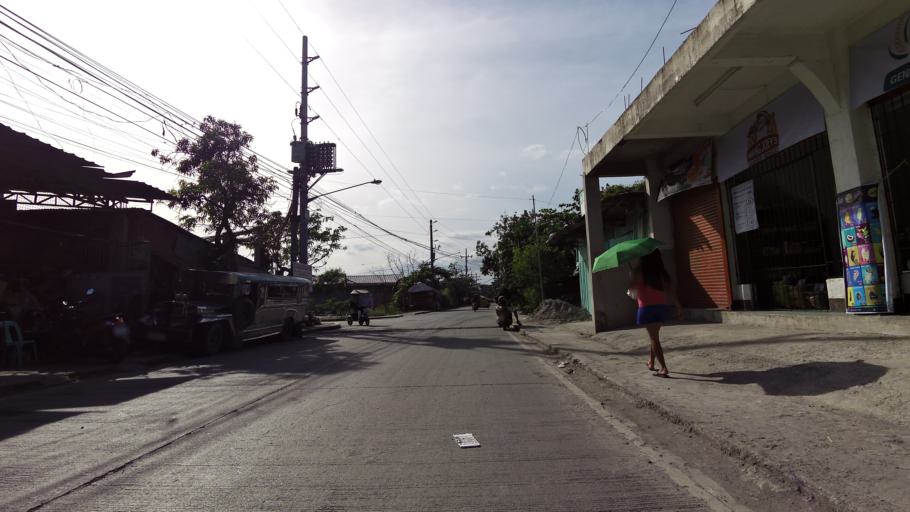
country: PH
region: Calabarzon
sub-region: Province of Rizal
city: Taytay
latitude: 14.5421
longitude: 121.1121
